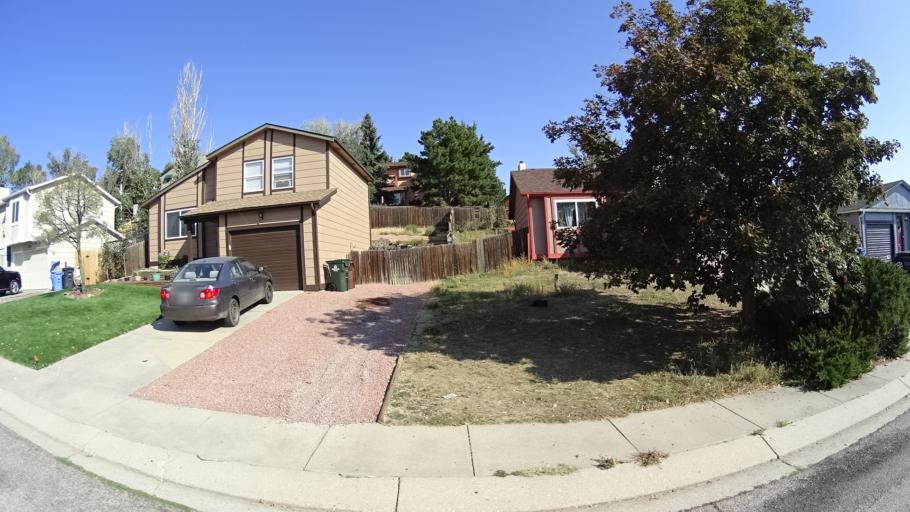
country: US
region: Colorado
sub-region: El Paso County
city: Cimarron Hills
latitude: 38.8894
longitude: -104.7234
